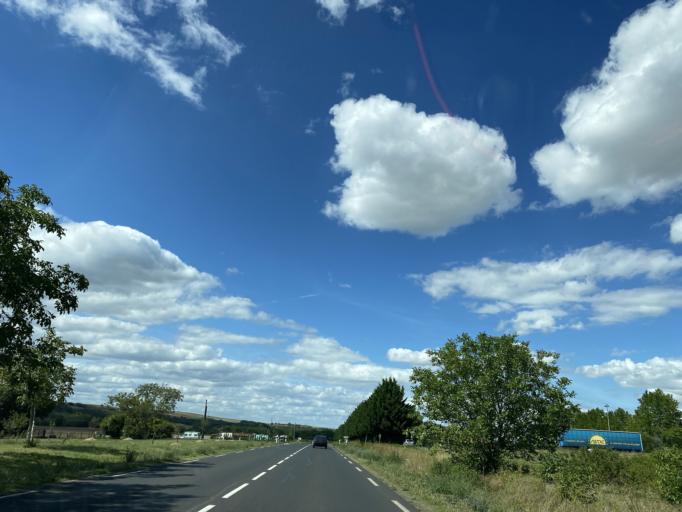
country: FR
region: Auvergne
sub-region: Departement du Puy-de-Dome
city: Mezel
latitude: 45.7529
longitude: 3.2368
